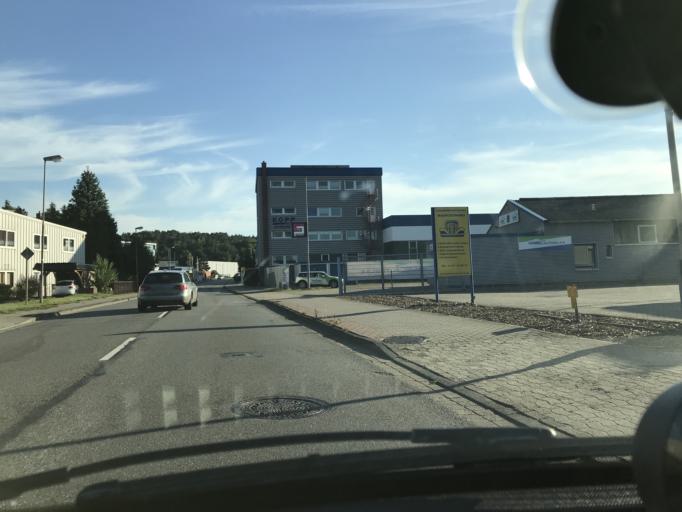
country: DE
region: Lower Saxony
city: Buxtehude
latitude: 53.4645
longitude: 9.7184
